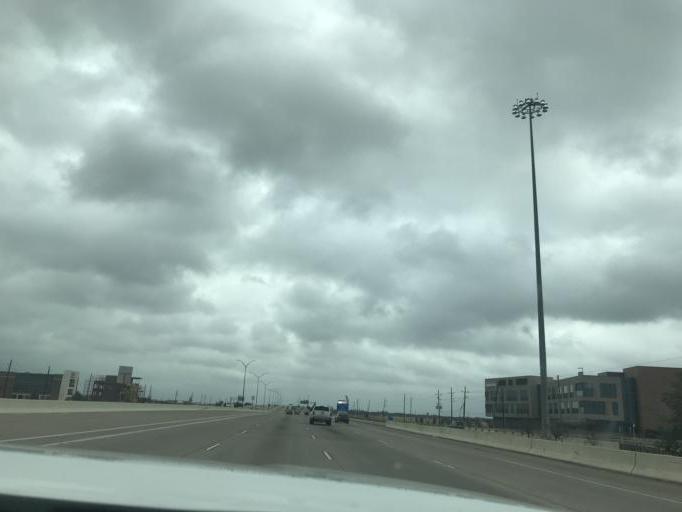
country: US
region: Texas
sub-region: Fort Bend County
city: Greatwood
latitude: 29.5766
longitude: -95.6545
